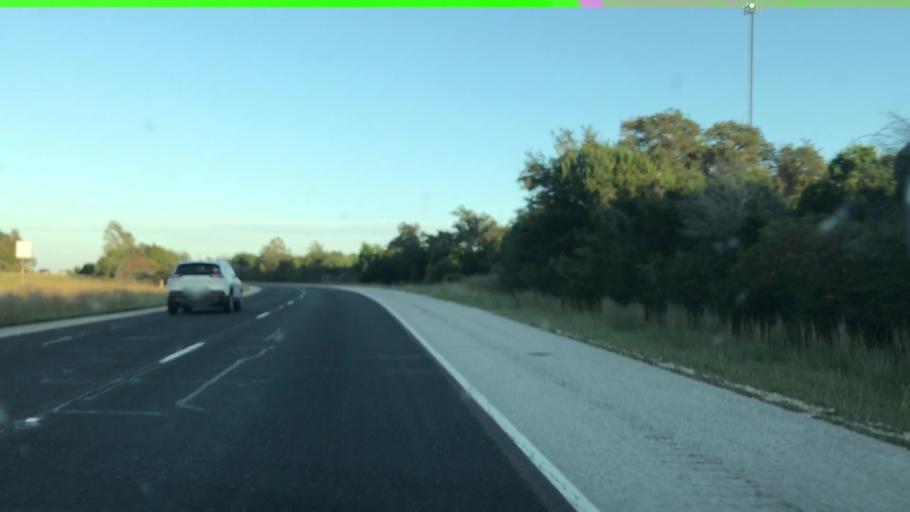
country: US
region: Texas
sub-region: Kerr County
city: Kerrville
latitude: 30.0677
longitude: -99.0753
